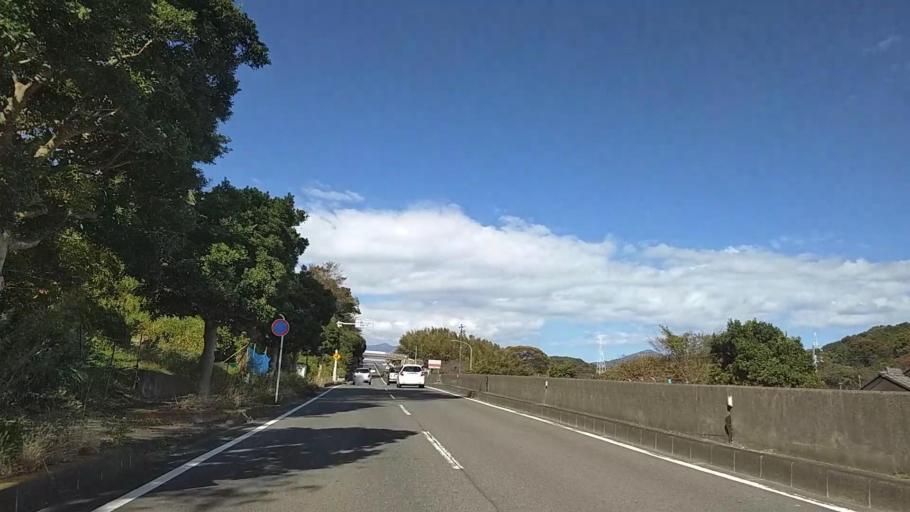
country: JP
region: Kanagawa
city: Ninomiya
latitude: 35.3173
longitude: 139.2414
